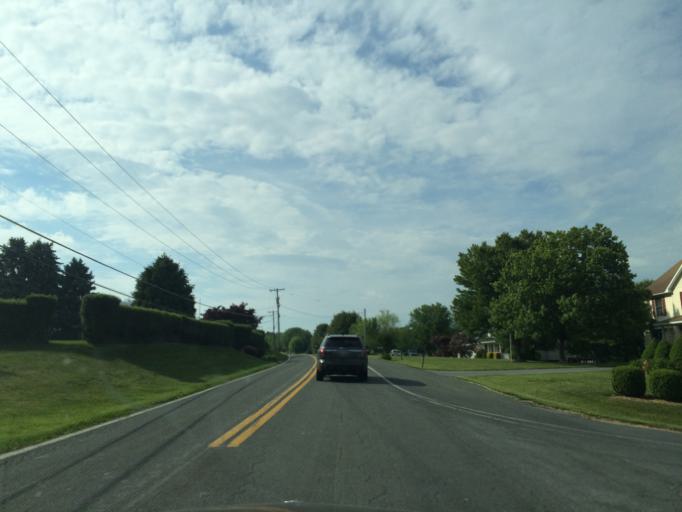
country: US
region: Maryland
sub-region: Carroll County
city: Eldersburg
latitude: 39.4893
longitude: -76.9301
